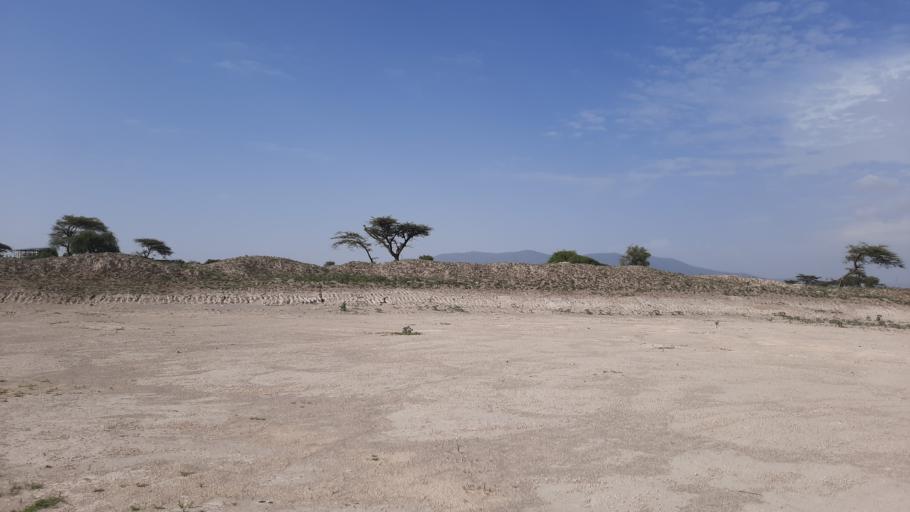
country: ET
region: Oromiya
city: Ziway
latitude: 7.6932
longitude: 38.6633
